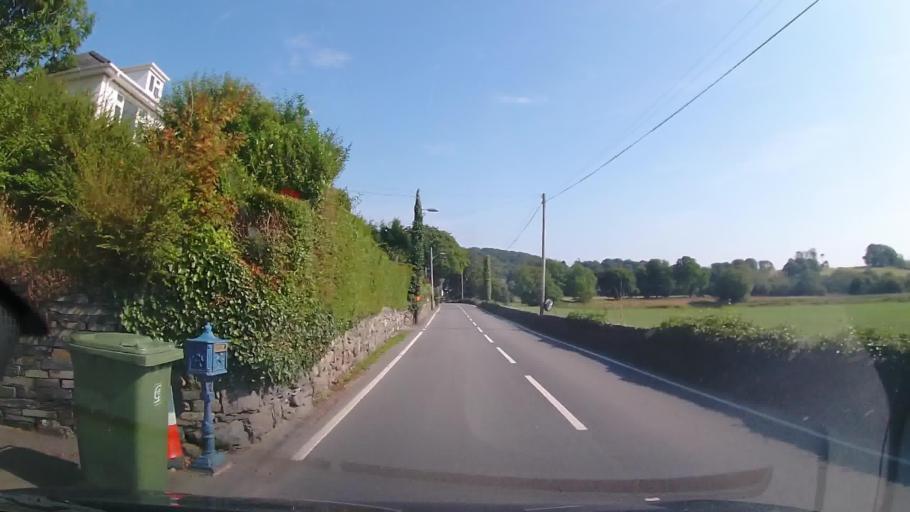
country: GB
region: Wales
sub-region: Gwynedd
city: Llanbedr
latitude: 52.8242
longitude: -4.1035
